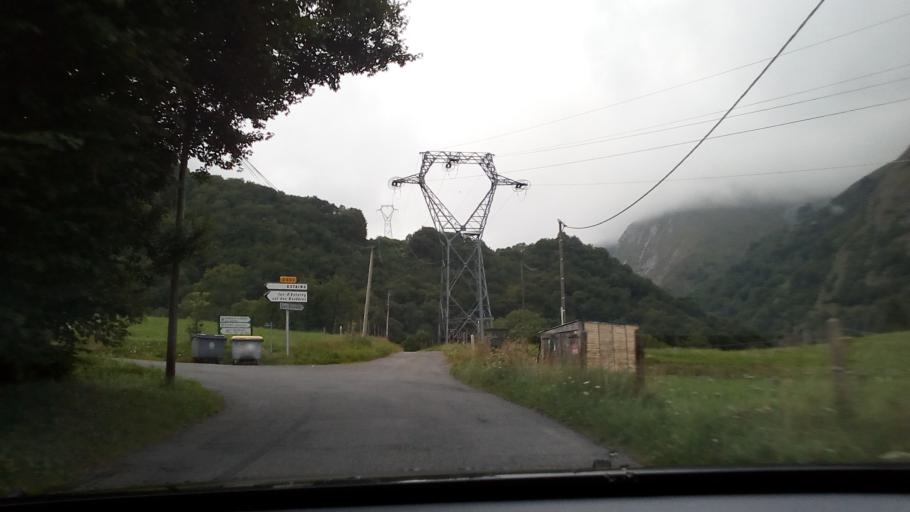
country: FR
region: Midi-Pyrenees
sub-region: Departement des Hautes-Pyrenees
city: Cauterets
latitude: 42.9455
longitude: -0.2196
